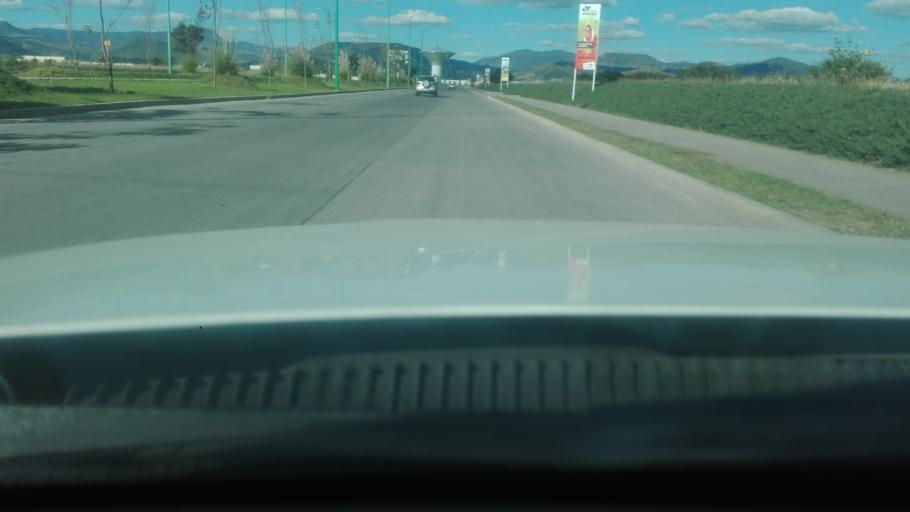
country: MX
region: Guanajuato
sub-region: Leon
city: Ladrilleras del Refugio
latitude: 21.0624
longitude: -101.5708
